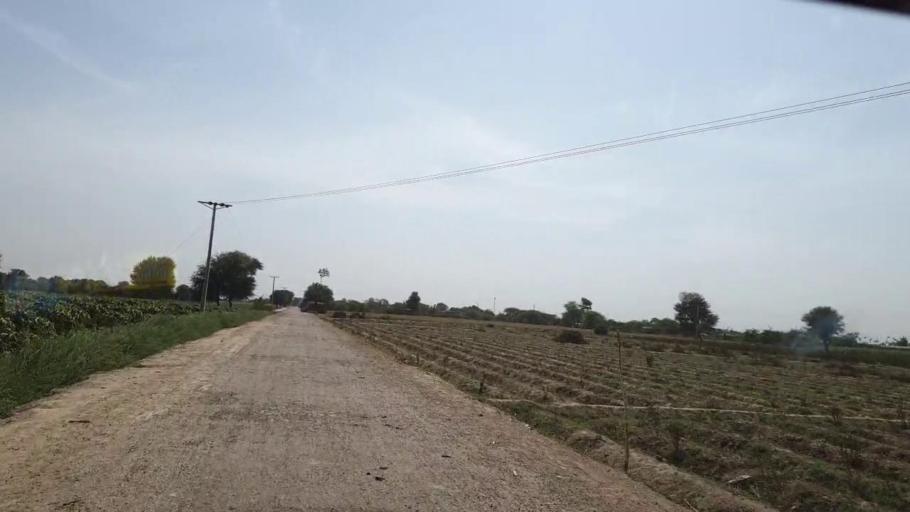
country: PK
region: Sindh
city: Kunri
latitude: 25.1147
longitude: 69.5682
